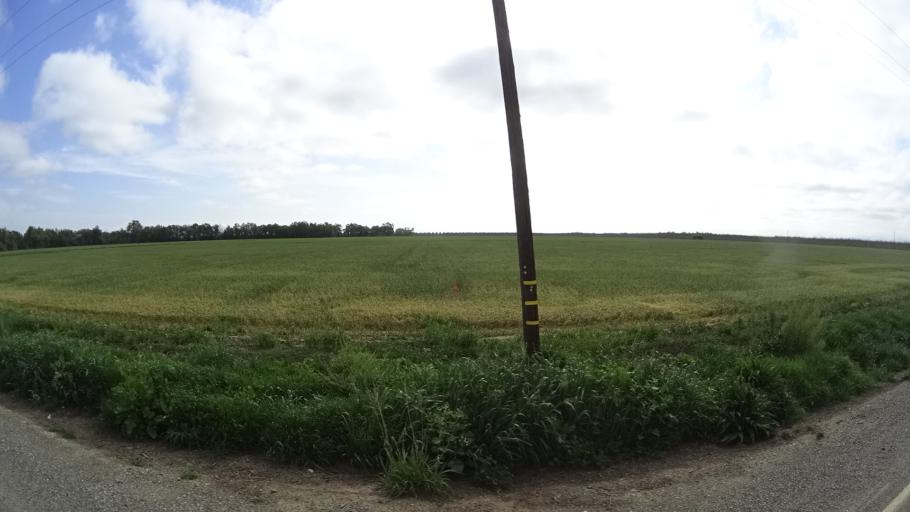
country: US
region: California
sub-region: Colusa County
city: Colusa
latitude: 39.4153
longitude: -121.9668
